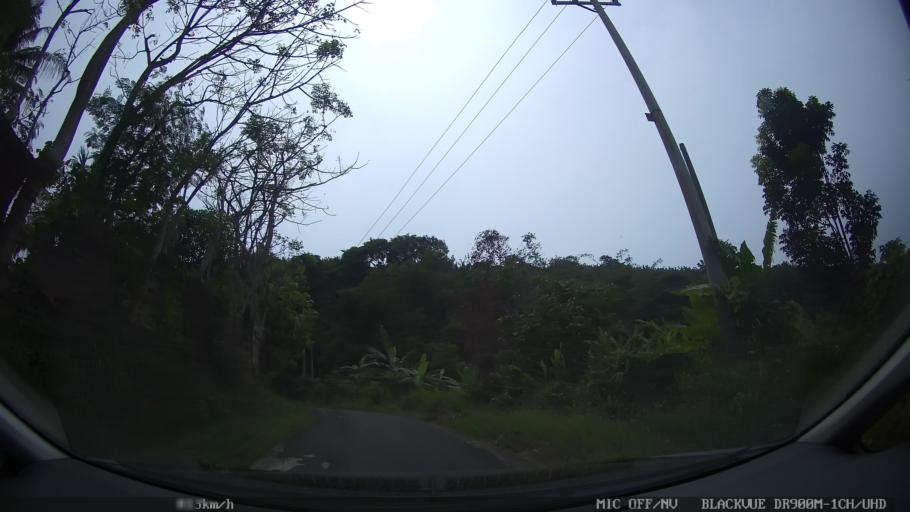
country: ID
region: Lampung
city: Bandarlampung
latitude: -5.4292
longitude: 105.3022
